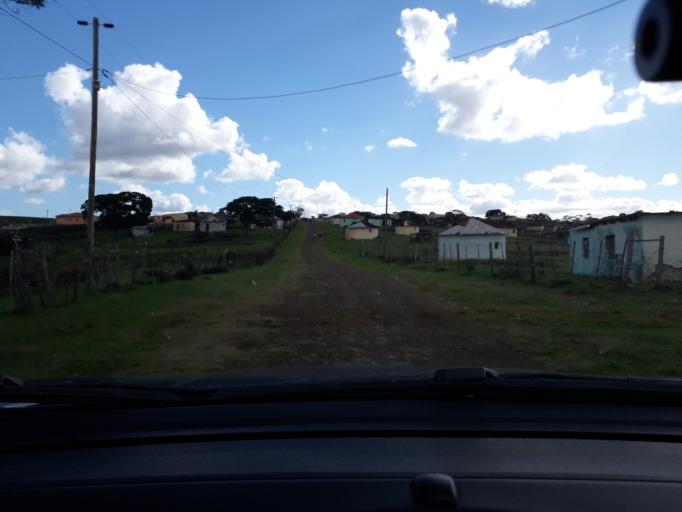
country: ZA
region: Eastern Cape
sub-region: Buffalo City Metropolitan Municipality
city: Bhisho
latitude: -33.1168
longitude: 27.4326
